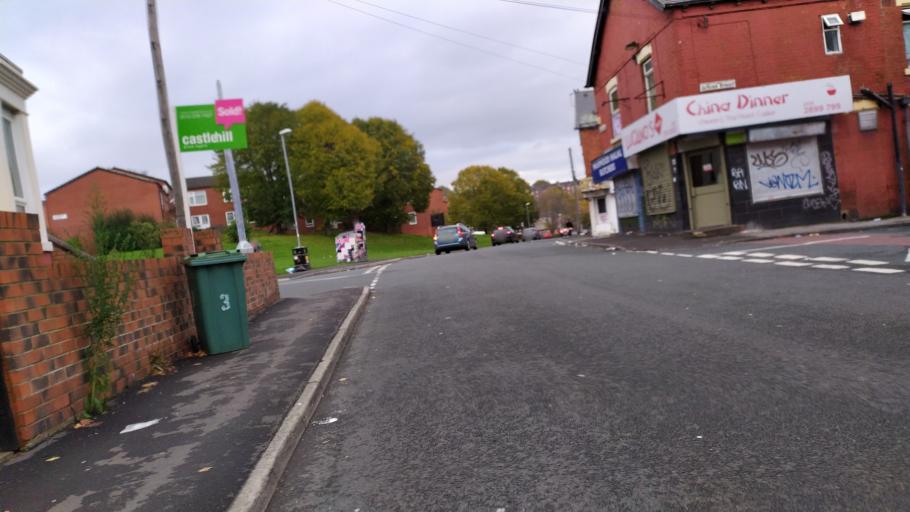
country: GB
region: England
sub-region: City and Borough of Leeds
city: Leeds
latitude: 53.8077
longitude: -1.5710
